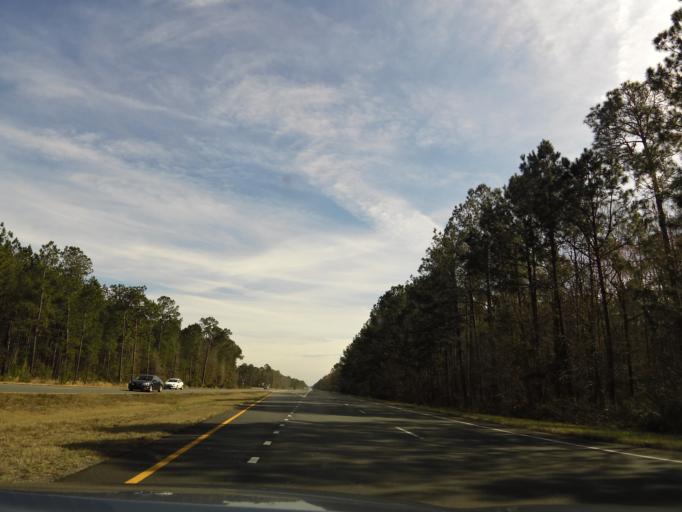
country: US
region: Georgia
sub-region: Glynn County
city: Dock Junction
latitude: 31.2069
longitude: -81.6959
